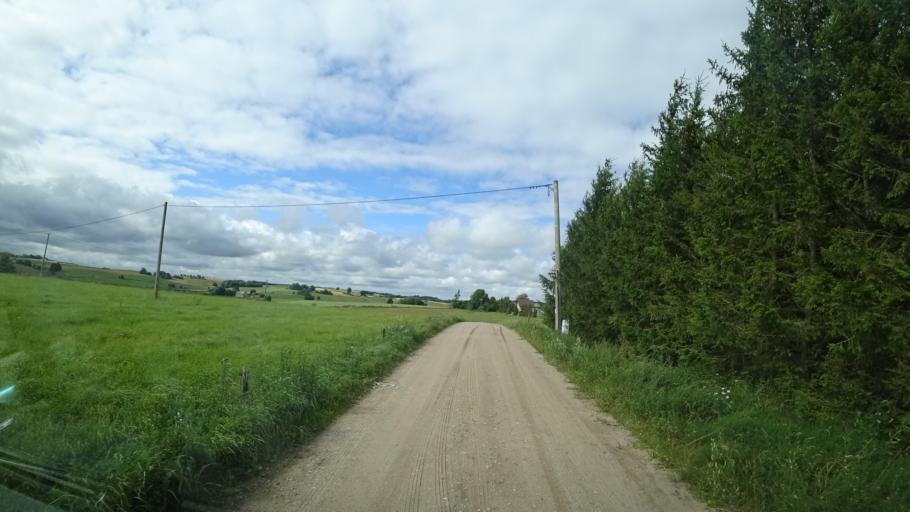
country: LT
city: Virbalis
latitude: 54.3757
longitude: 22.9024
